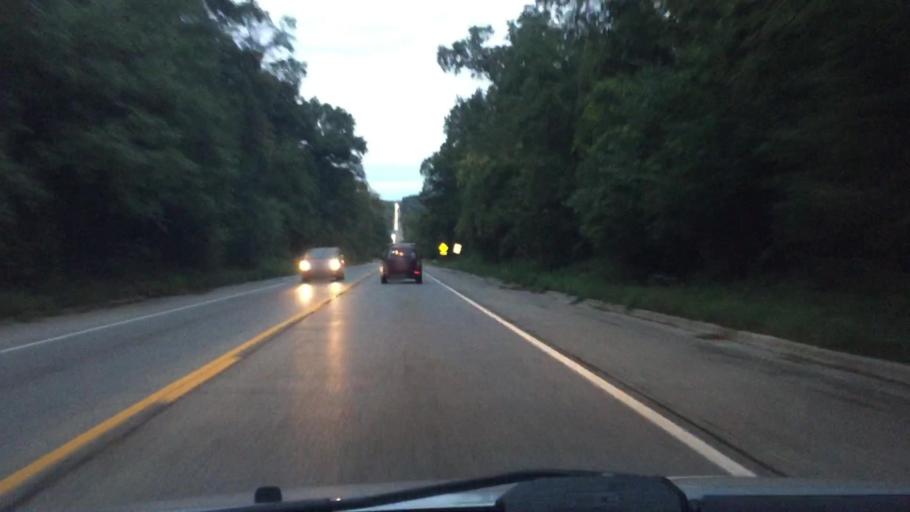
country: US
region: Illinois
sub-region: McHenry County
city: Prairie Grove
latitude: 42.2613
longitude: -88.2867
